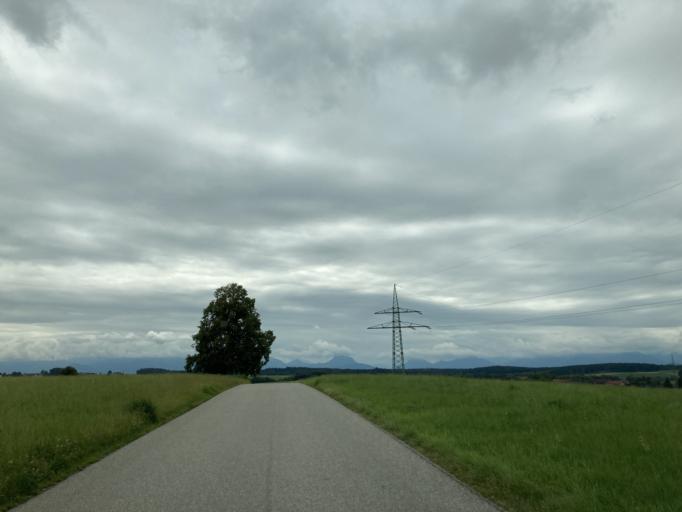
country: DE
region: Bavaria
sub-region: Upper Bavaria
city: Vogtareuth
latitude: 47.9434
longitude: 12.1763
